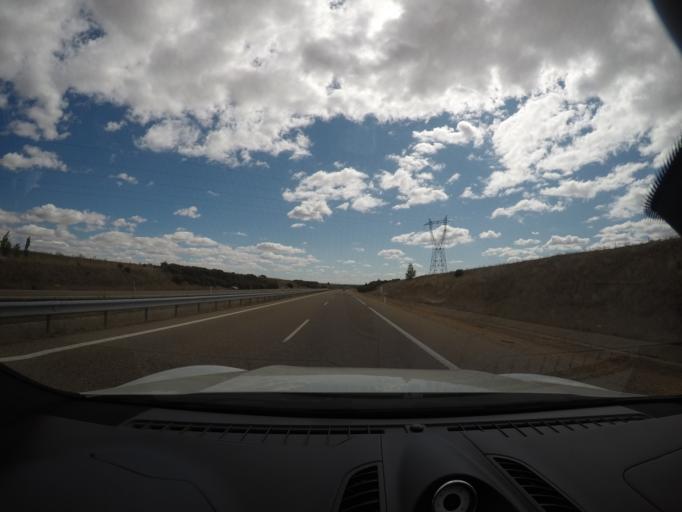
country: ES
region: Castille and Leon
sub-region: Provincia de Leon
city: Villamanan
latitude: 42.3088
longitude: -5.5969
